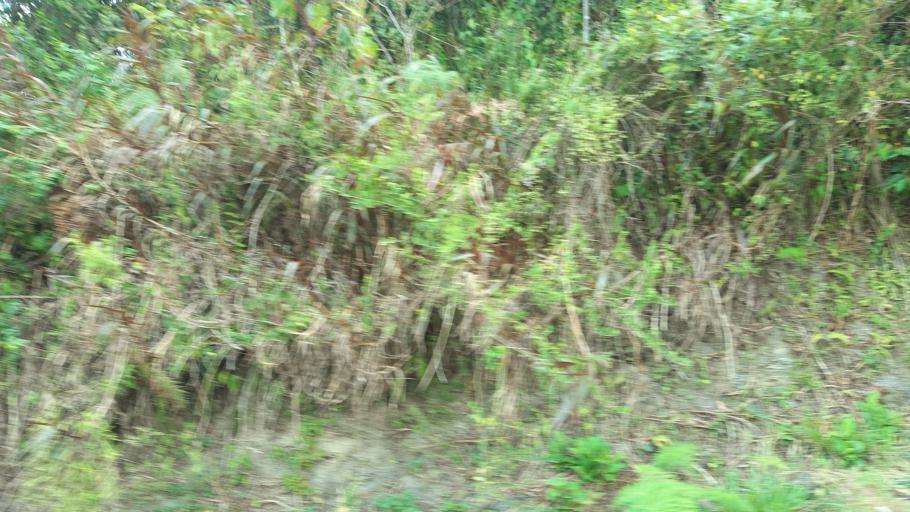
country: CO
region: Boyaca
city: Moniquira
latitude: 5.8419
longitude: -73.5852
